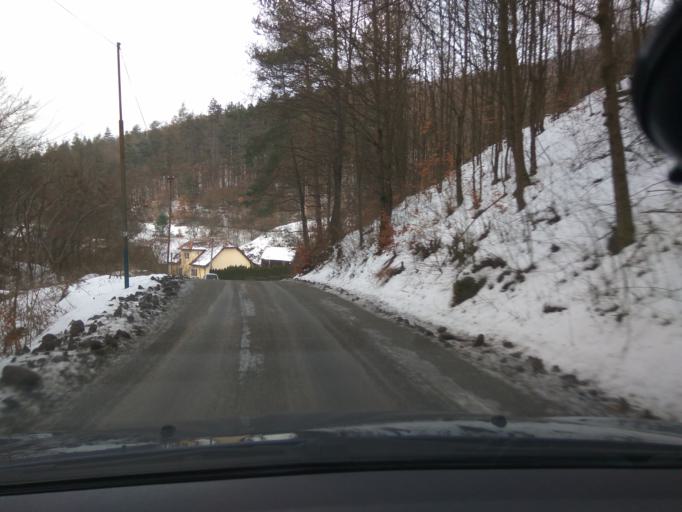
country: SK
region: Banskobystricky
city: Zarnovica
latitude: 48.4816
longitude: 18.7482
